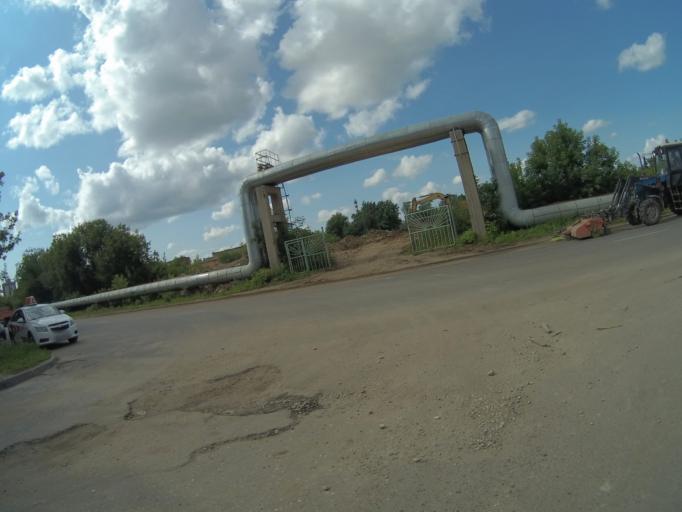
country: RU
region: Vladimir
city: Vladimir
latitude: 56.1446
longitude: 40.4012
